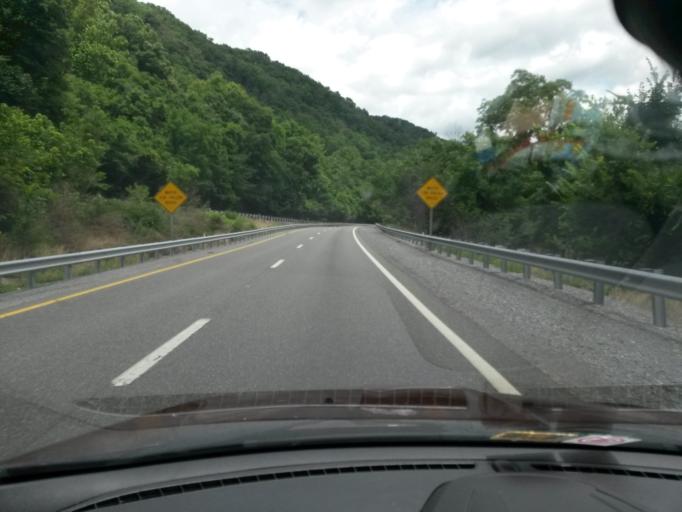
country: US
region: Virginia
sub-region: Giles County
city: Narrows
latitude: 37.3869
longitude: -80.8400
